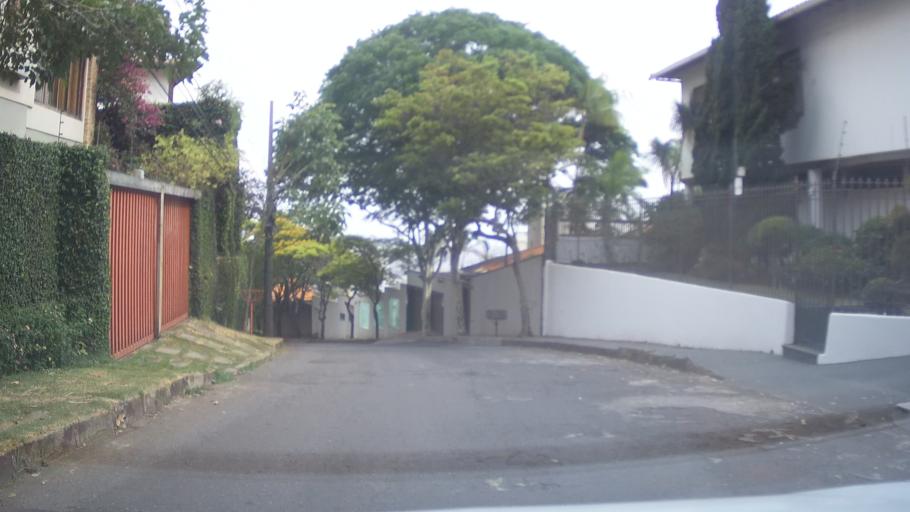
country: BR
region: Minas Gerais
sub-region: Belo Horizonte
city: Belo Horizonte
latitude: -19.9523
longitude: -43.9175
